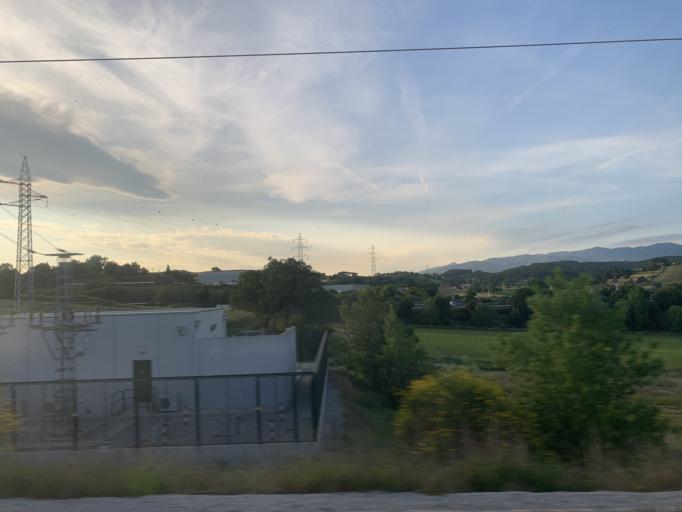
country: ES
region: Catalonia
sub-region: Provincia de Barcelona
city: La Roca del Valles
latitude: 41.5950
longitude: 2.3214
